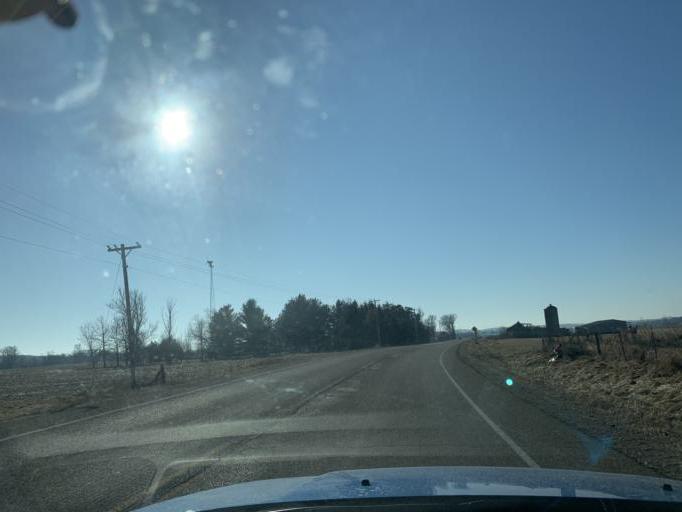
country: US
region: Wisconsin
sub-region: Dane County
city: Belleville
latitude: 42.9044
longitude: -89.5358
